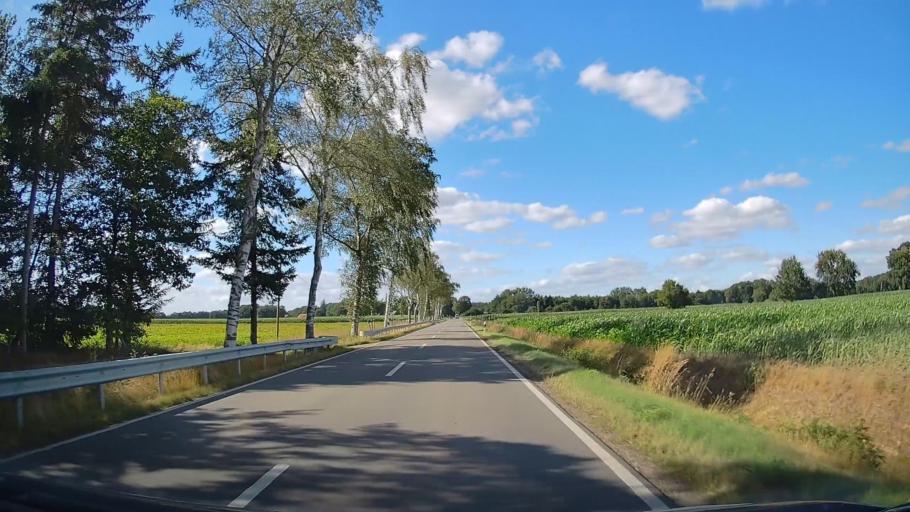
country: DE
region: Lower Saxony
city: Loningen
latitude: 52.7001
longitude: 7.7590
